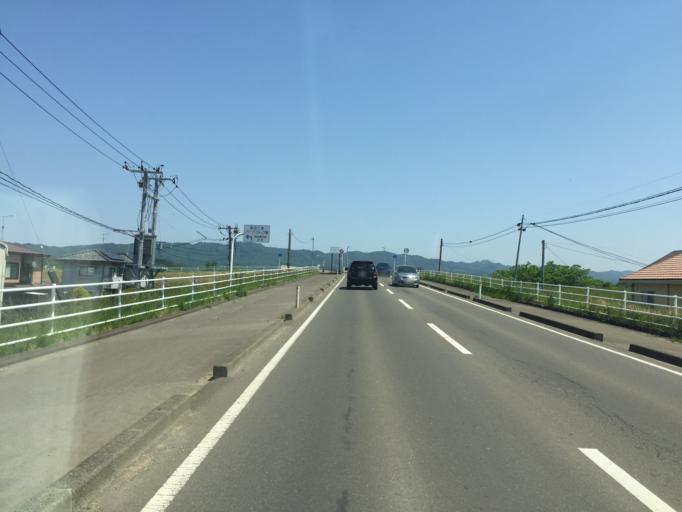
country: JP
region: Miyagi
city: Kakuda
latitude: 37.9740
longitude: 140.7959
